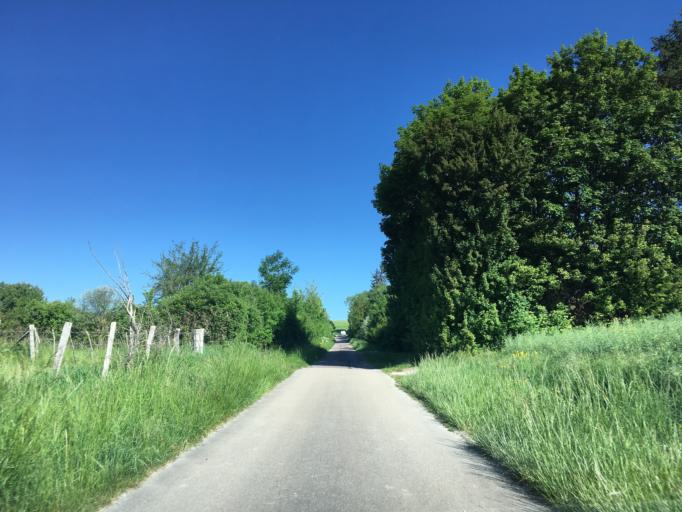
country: FR
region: Bourgogne
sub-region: Departement de l'Yonne
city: Aillant-sur-Tholon
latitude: 47.8261
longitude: 3.3423
